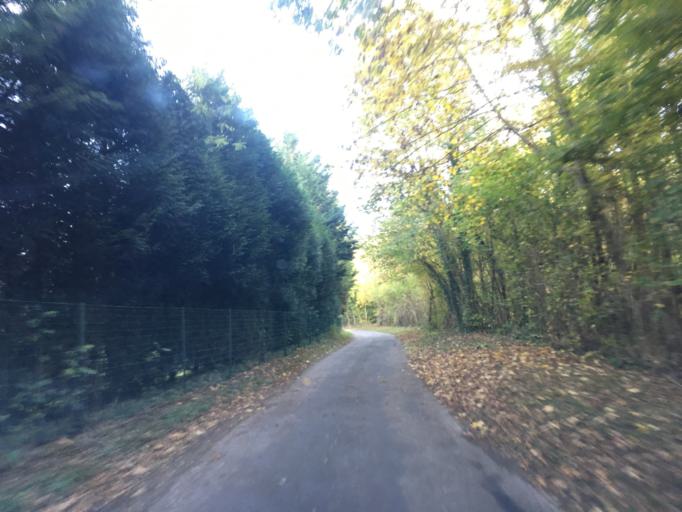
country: FR
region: Haute-Normandie
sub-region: Departement de l'Eure
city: Heudreville-sur-Eure
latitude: 49.1112
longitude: 1.2252
